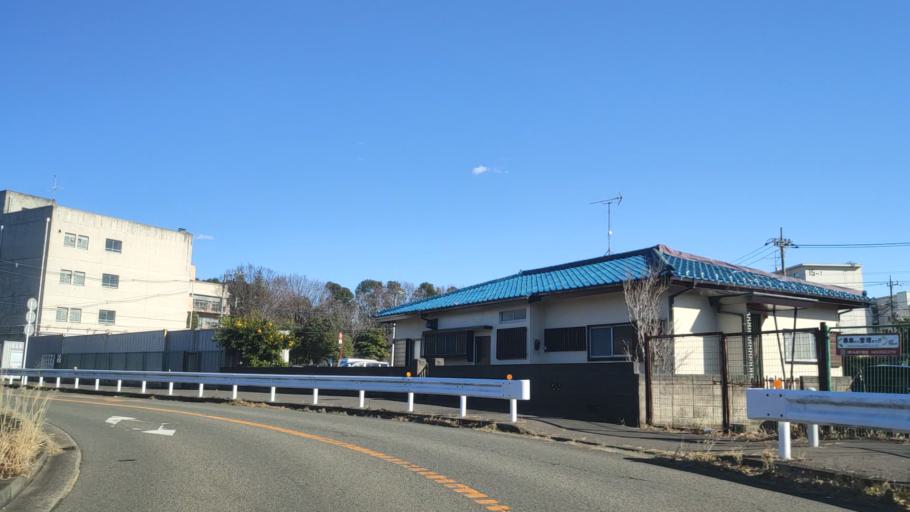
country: JP
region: Kanagawa
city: Minami-rinkan
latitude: 35.5032
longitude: 139.5294
